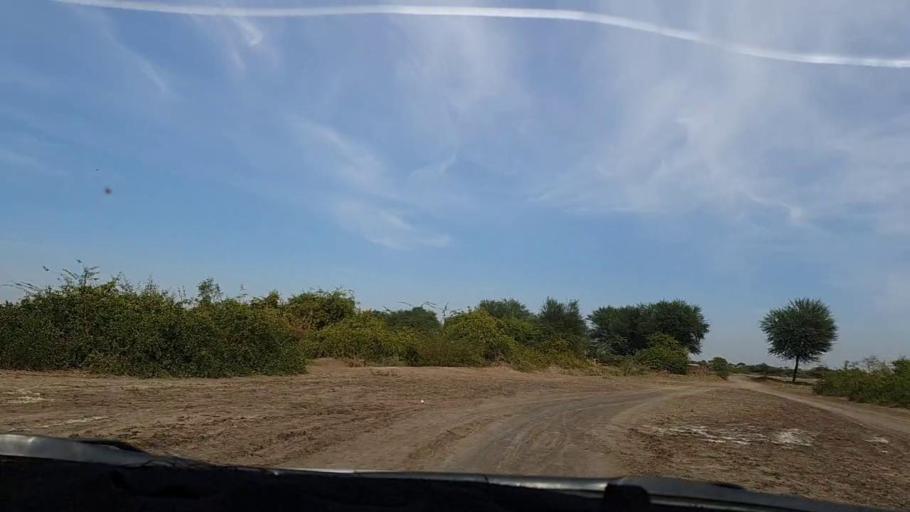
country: PK
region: Sindh
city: Dhoro Naro
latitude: 25.4739
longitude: 69.4750
